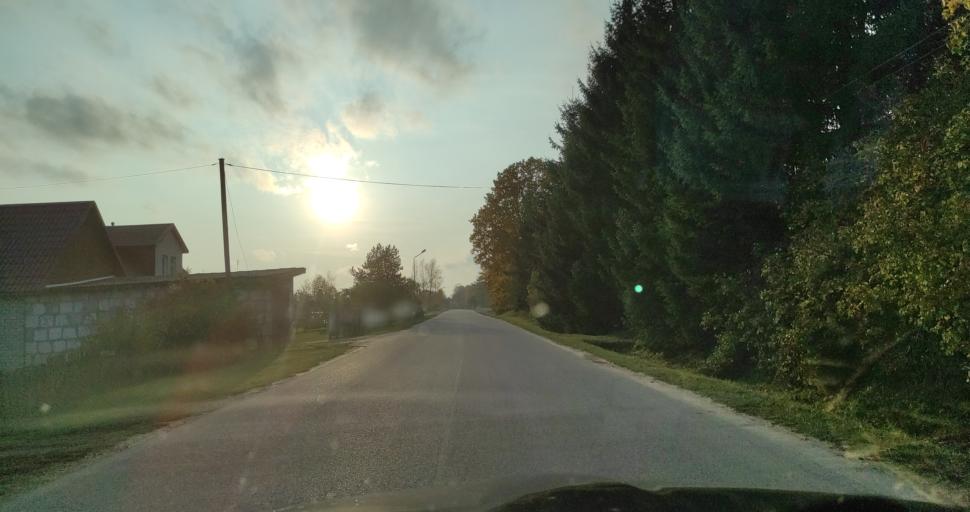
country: LV
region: Vainode
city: Vainode
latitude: 56.4204
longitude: 21.8661
